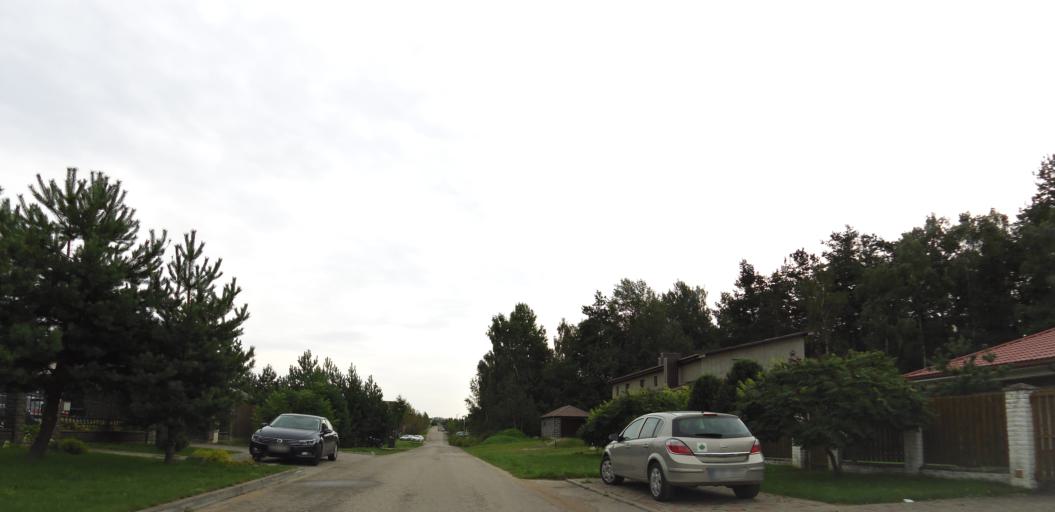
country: LT
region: Vilnius County
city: Pasilaiciai
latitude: 54.7536
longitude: 25.2301
